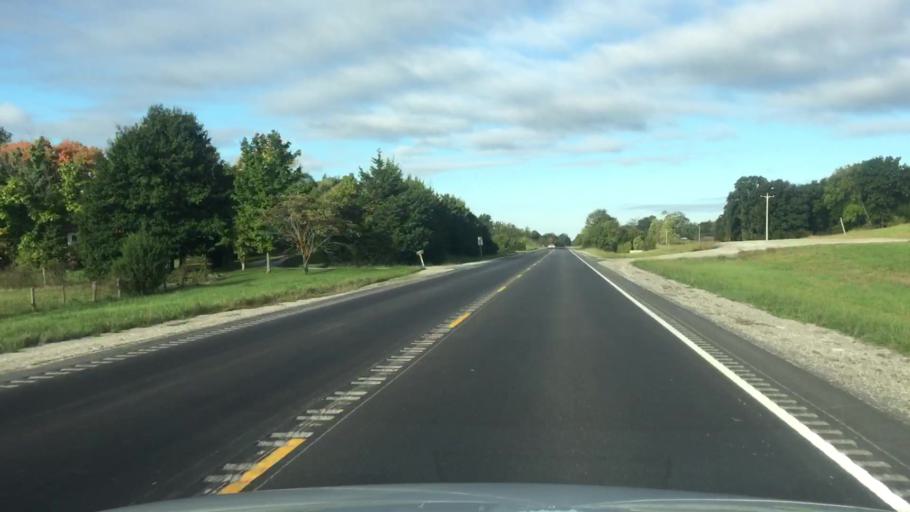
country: US
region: Missouri
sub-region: Boone County
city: Columbia
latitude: 38.9892
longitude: -92.4963
